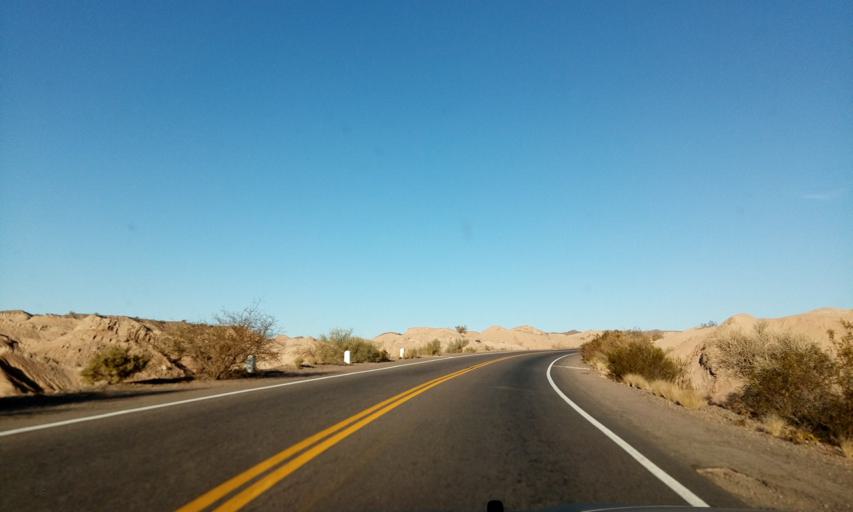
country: AR
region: San Juan
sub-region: Departamento de Rivadavia
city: Rivadavia
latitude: -31.4489
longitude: -68.6392
